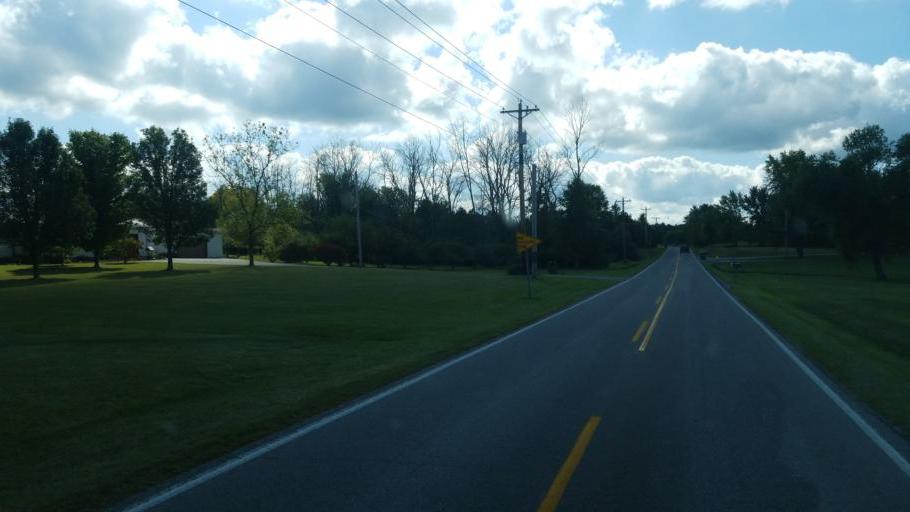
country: US
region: Ohio
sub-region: Lorain County
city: Lagrange
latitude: 41.1662
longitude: -82.0946
